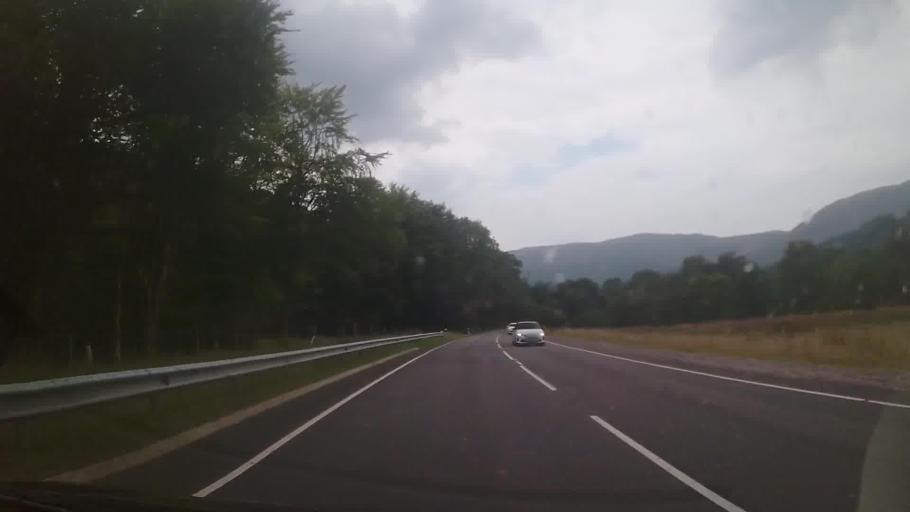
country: GB
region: Scotland
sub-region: Highland
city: Fort William
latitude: 56.6767
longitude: -5.0893
